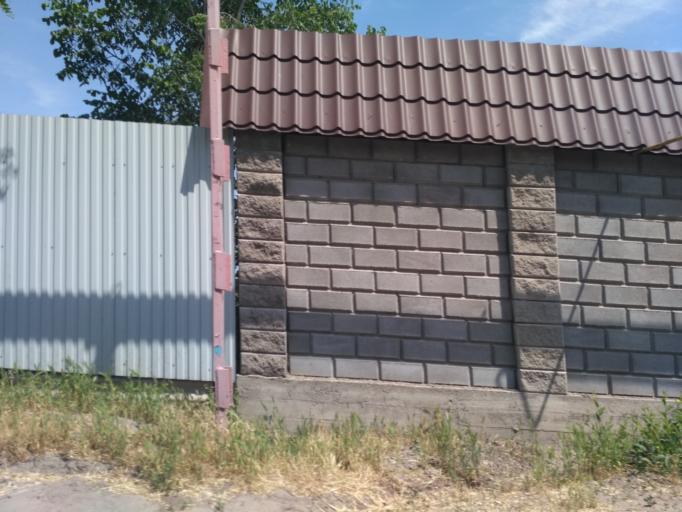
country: KZ
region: Almaty Oblysy
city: Burunday
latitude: 43.1874
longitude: 76.6197
